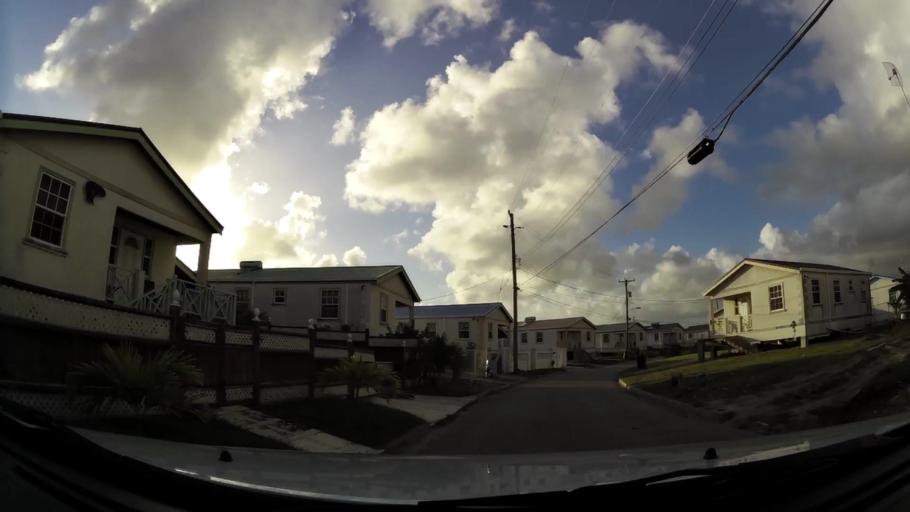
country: BB
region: Saint Philip
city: Crane
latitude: 13.1130
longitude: -59.4766
